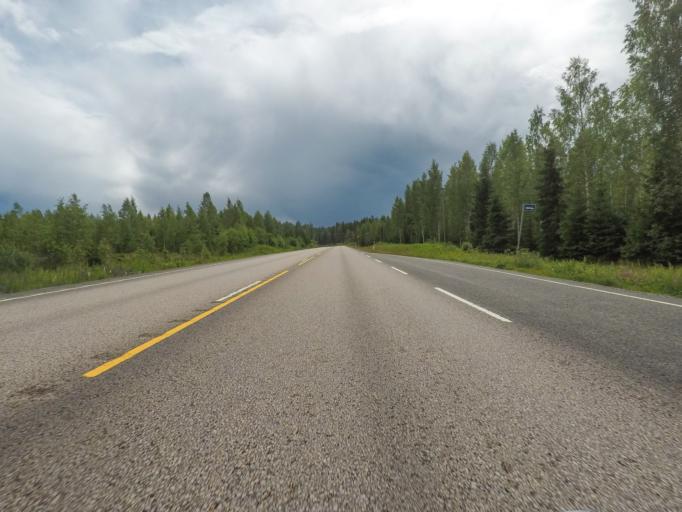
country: FI
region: Central Finland
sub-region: Jyvaeskylae
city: Toivakka
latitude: 62.0638
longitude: 26.0464
